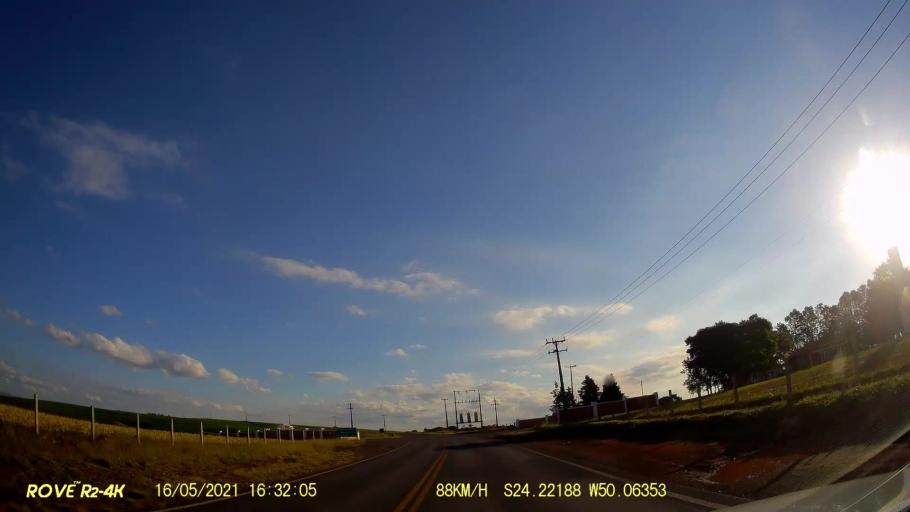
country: BR
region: Parana
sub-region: Pirai Do Sul
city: Pirai do Sul
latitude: -24.2226
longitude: -50.0637
